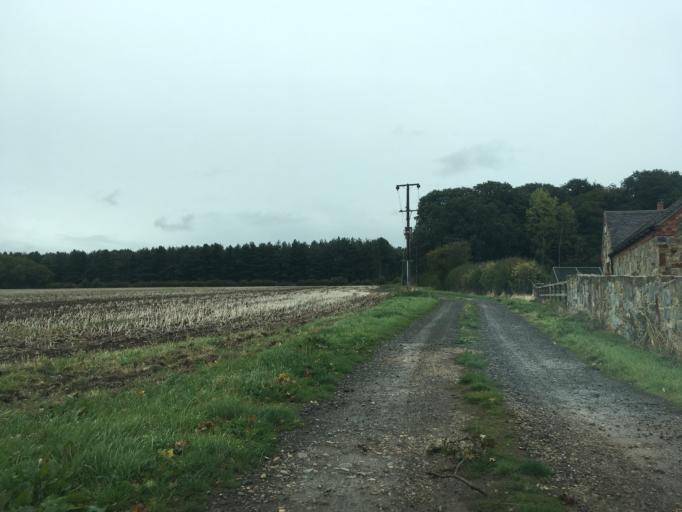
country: GB
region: England
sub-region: Nottinghamshire
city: Gotham
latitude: 52.8462
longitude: -1.2021
